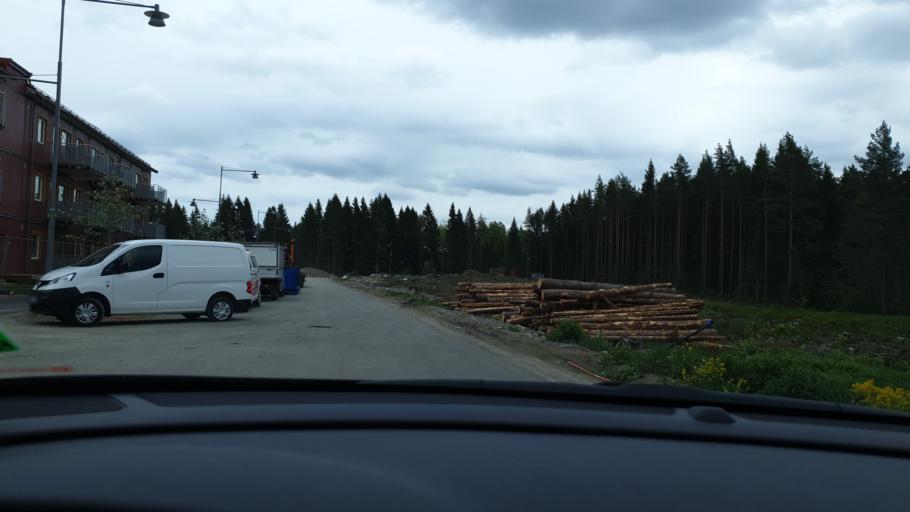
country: SE
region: Gaevleborg
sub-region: Gavle Kommun
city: Gavle
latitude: 60.6401
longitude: 17.1510
